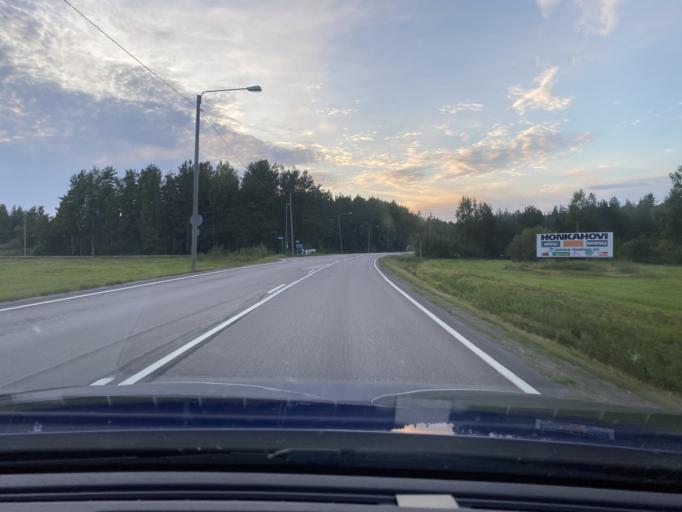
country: FI
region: Satakunta
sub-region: Pohjois-Satakunta
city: Honkajoki
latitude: 61.9256
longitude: 22.2444
